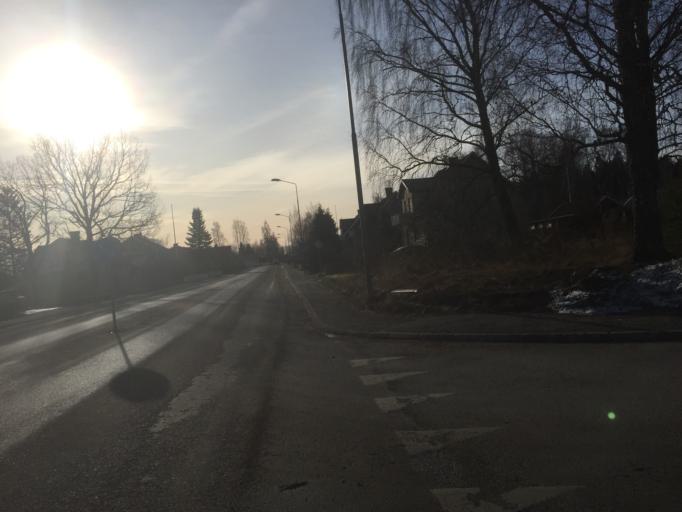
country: SE
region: Joenkoeping
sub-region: Aneby Kommun
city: Aneby
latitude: 57.8412
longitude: 14.8041
